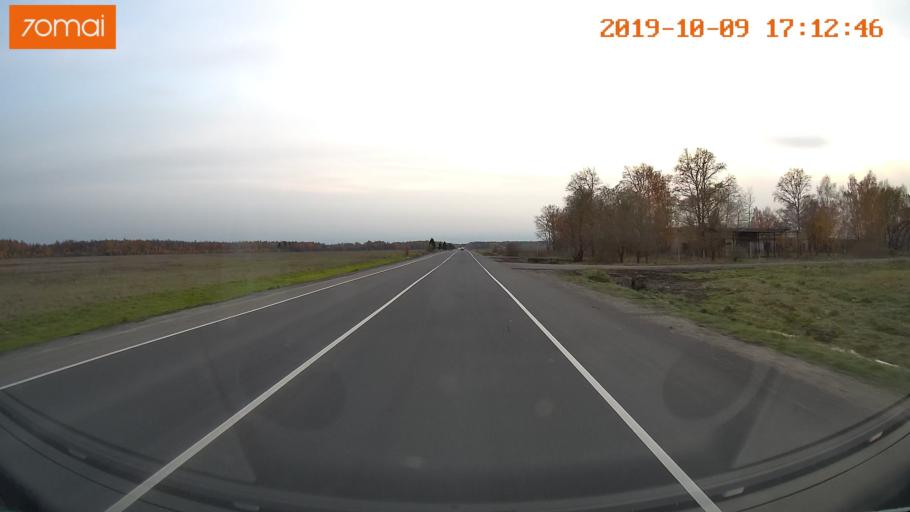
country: RU
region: Ivanovo
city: Privolzhsk
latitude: 57.3241
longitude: 41.2361
